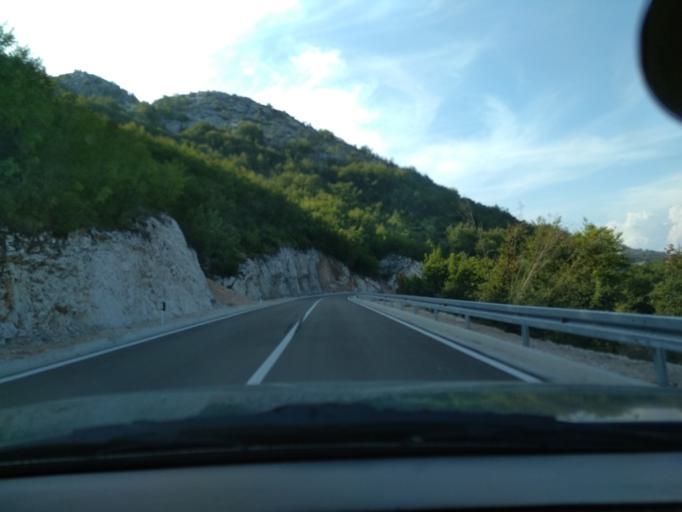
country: ME
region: Cetinje
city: Cetinje
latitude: 42.4196
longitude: 18.8752
